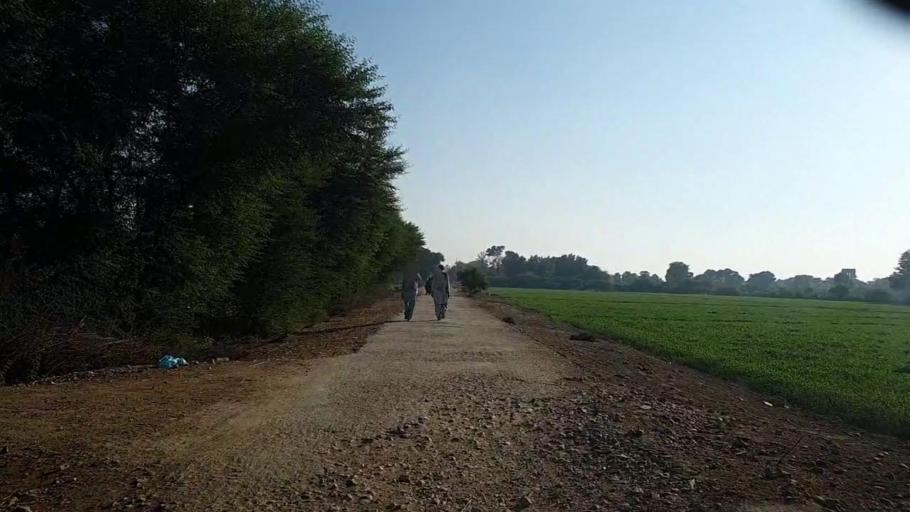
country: PK
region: Sindh
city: Darya Khan Marri
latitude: 26.6994
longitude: 68.3625
